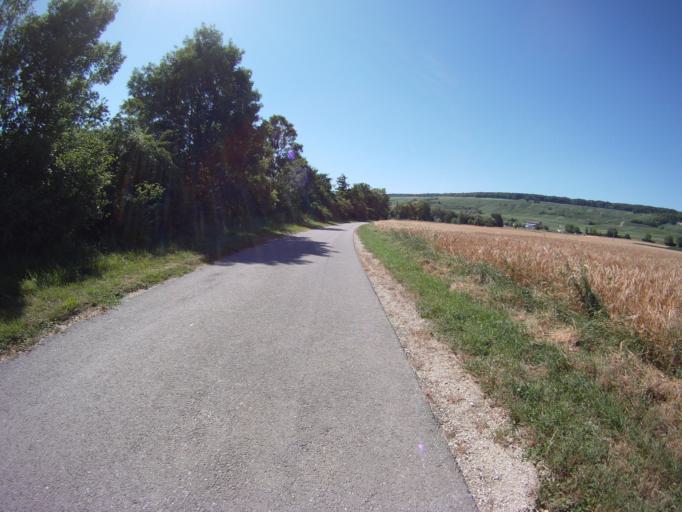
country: FR
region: Champagne-Ardenne
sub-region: Departement de la Marne
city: Dormans
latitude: 49.0897
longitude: 3.6556
